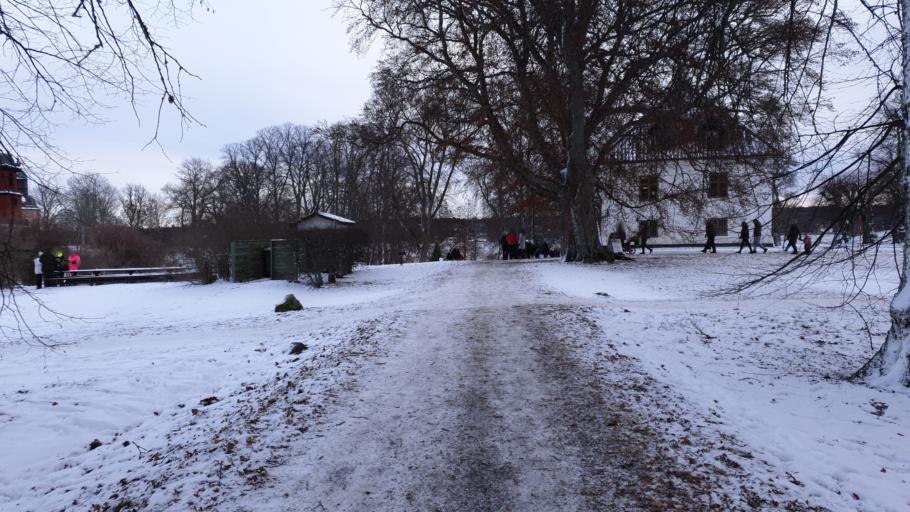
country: SE
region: Stockholm
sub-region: Sigtuna Kommun
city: Sigtuna
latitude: 59.7041
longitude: 17.6206
